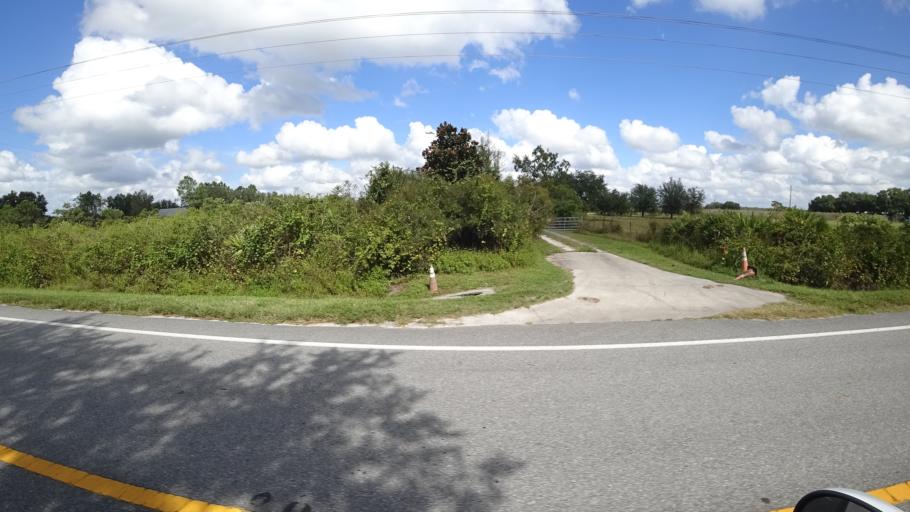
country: US
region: Florida
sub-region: Hillsborough County
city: Wimauma
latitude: 27.4599
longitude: -82.1175
